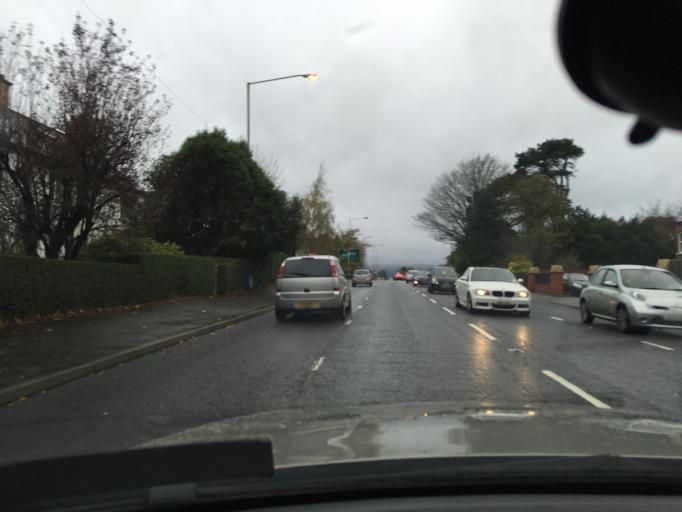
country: GB
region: Northern Ireland
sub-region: Castlereagh District
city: Castlereagh
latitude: 54.5944
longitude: -5.8509
